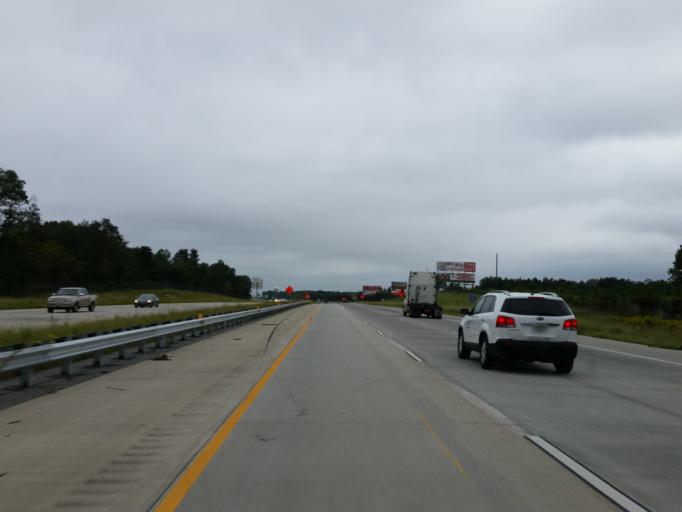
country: US
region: Georgia
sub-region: Dooly County
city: Vienna
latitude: 32.1165
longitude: -83.7622
